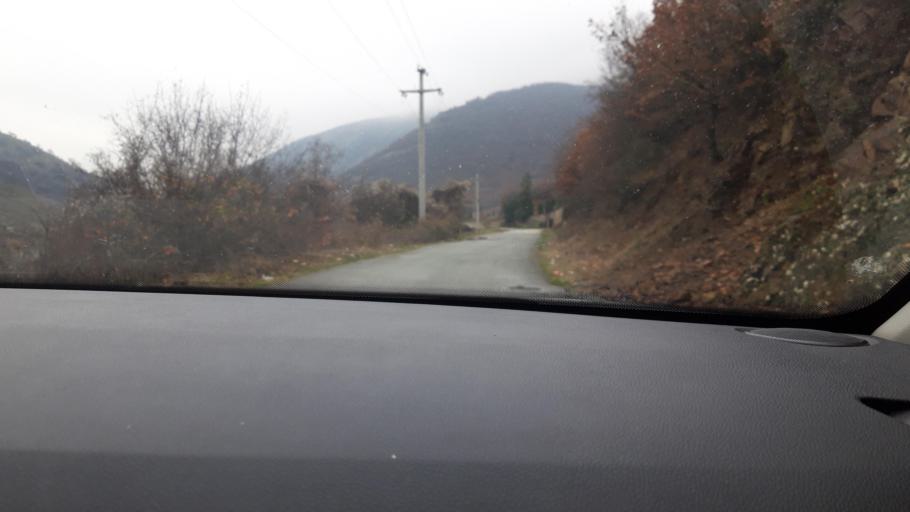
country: MK
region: Opstina Lipkovo
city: Lipkovo
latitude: 42.1716
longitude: 21.5695
